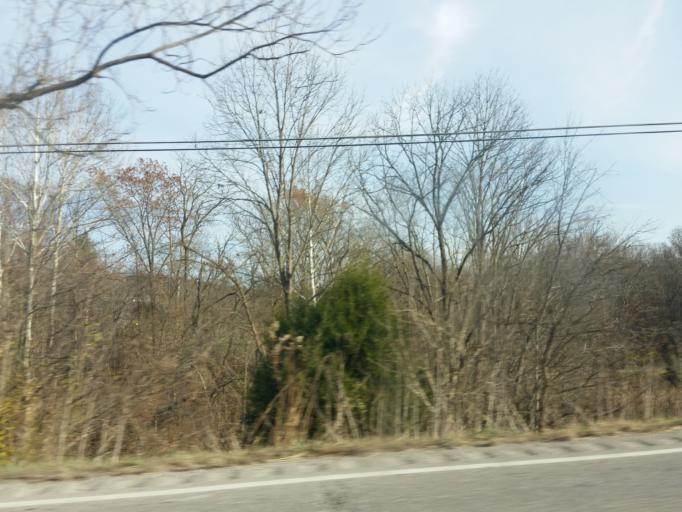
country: US
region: Kentucky
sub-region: Pendleton County
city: Falmouth
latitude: 38.7597
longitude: -84.3529
